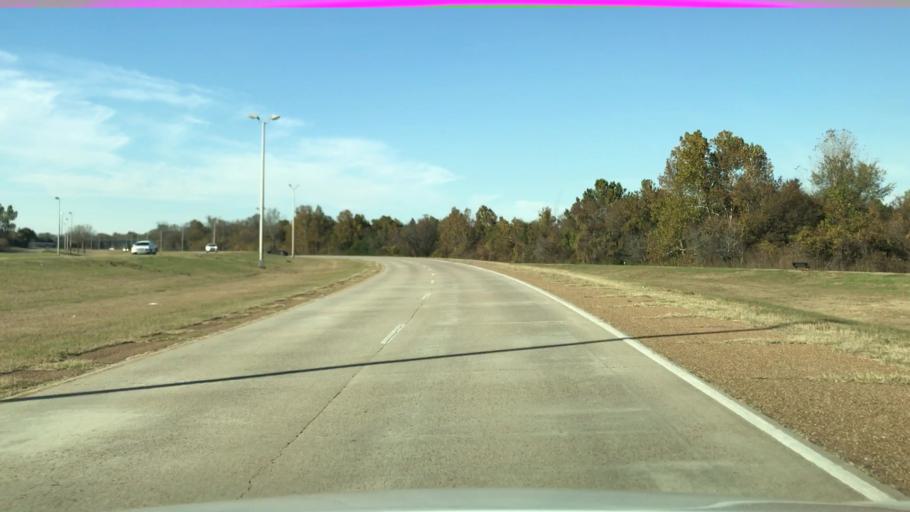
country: US
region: Louisiana
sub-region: Bossier Parish
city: Bossier City
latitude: 32.4835
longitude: -93.6935
